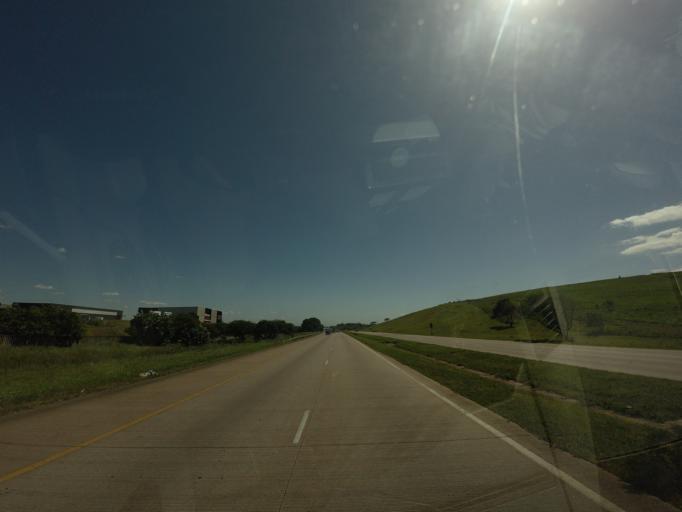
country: ZA
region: KwaZulu-Natal
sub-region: iLembe District Municipality
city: Ballitoville
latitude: -29.5088
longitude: 31.2058
